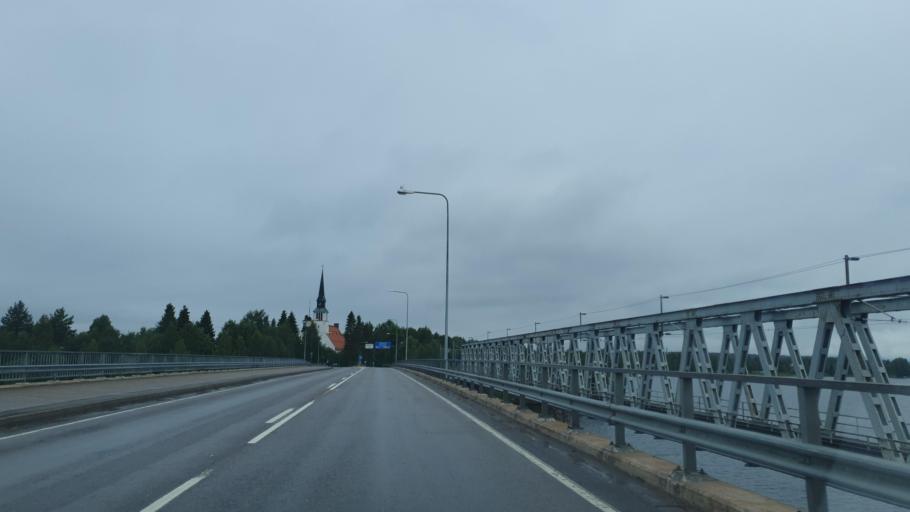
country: FI
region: Lapland
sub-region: Itae-Lappi
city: Kemijaervi
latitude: 66.7158
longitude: 27.4478
